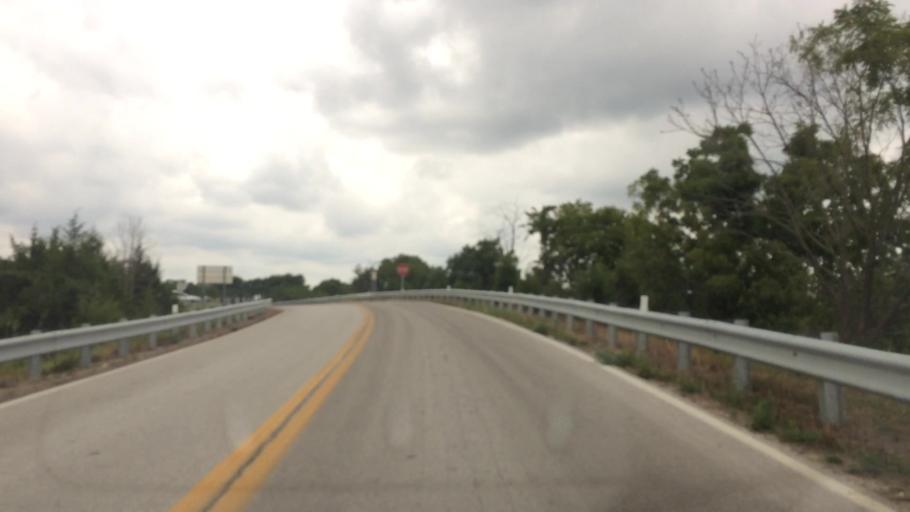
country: US
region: Missouri
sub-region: Webster County
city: Marshfield
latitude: 37.3041
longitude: -92.9988
